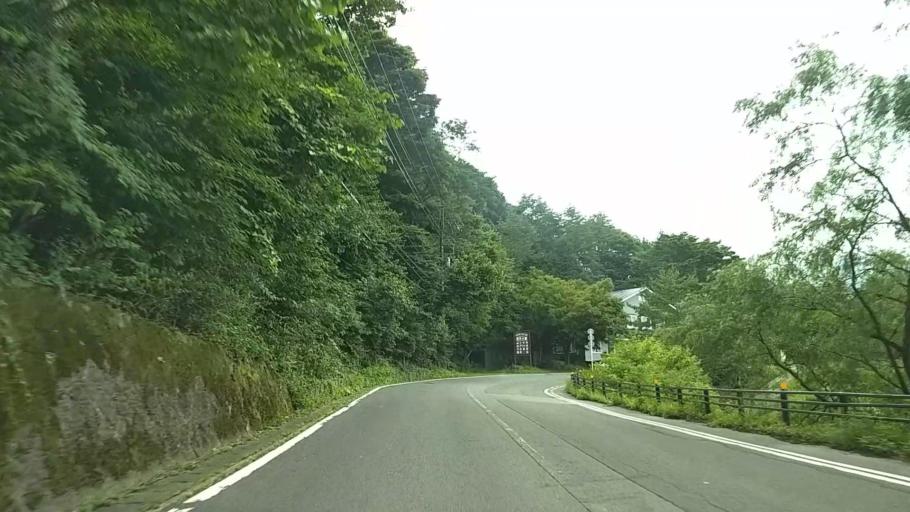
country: JP
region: Yamanashi
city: Fujikawaguchiko
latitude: 35.4914
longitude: 138.6835
